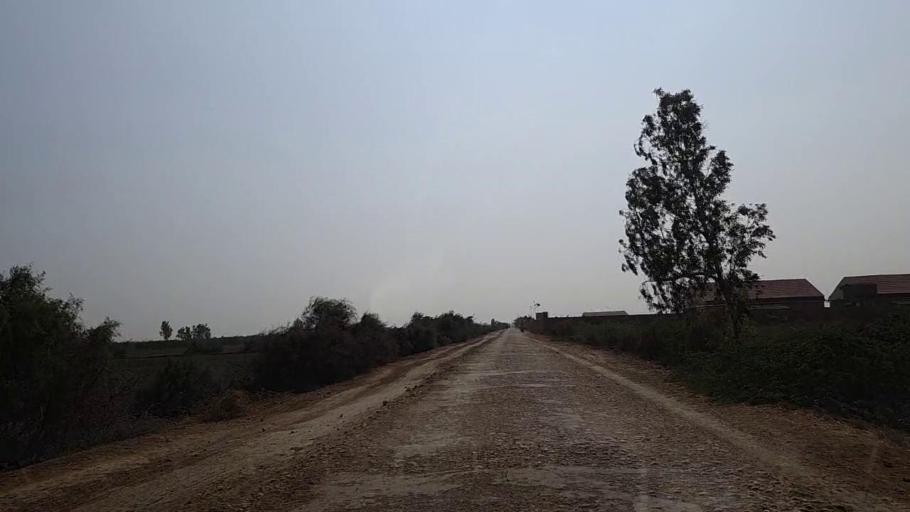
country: PK
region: Sindh
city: Thatta
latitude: 24.7096
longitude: 67.7674
